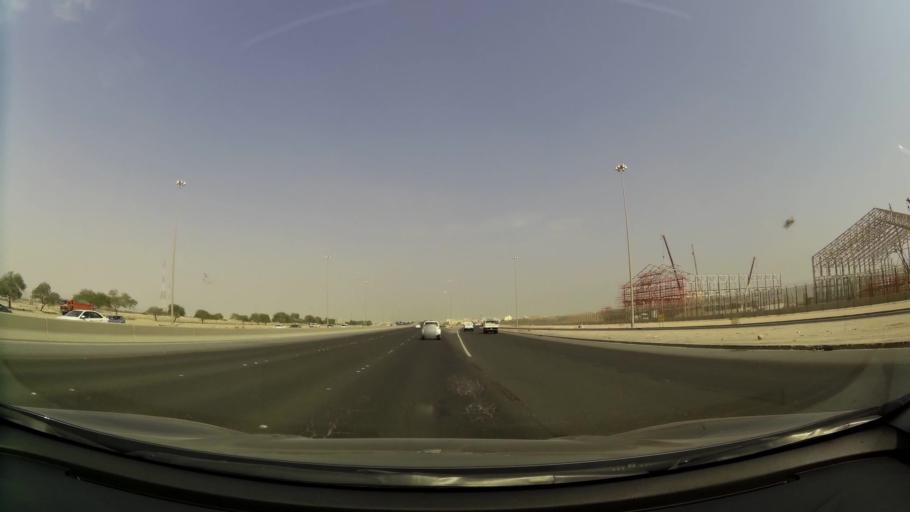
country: KW
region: Al Ahmadi
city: Al Fahahil
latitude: 29.0666
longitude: 48.1102
